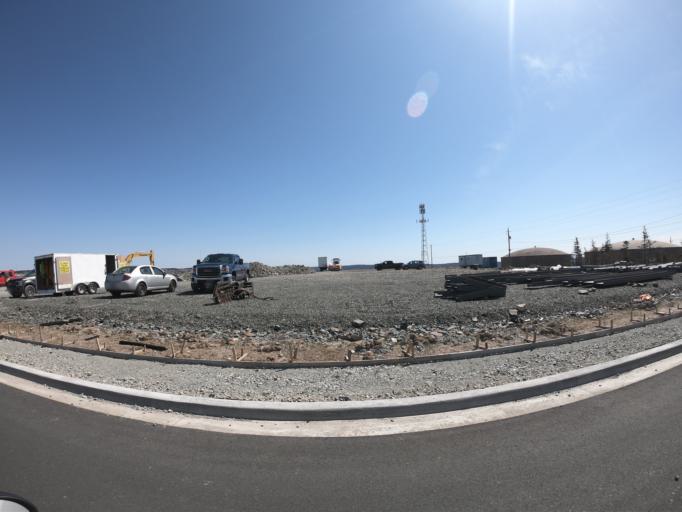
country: CA
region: Newfoundland and Labrador
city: Mount Pearl
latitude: 47.5072
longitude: -52.8325
